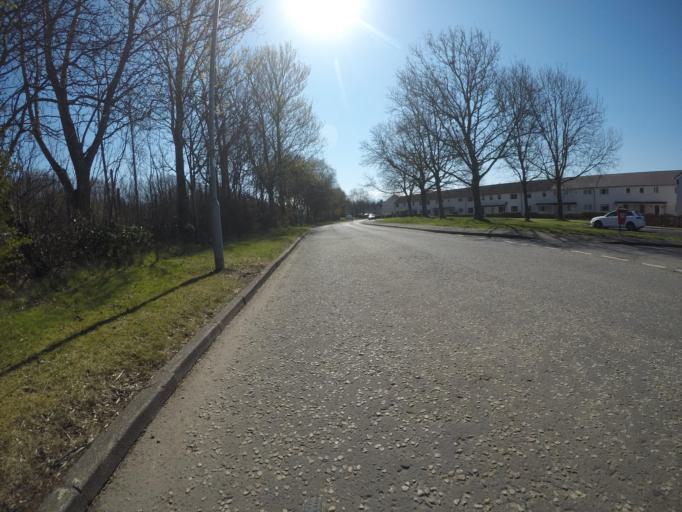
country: GB
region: Scotland
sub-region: North Ayrshire
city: Irvine
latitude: 55.6253
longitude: -4.6529
